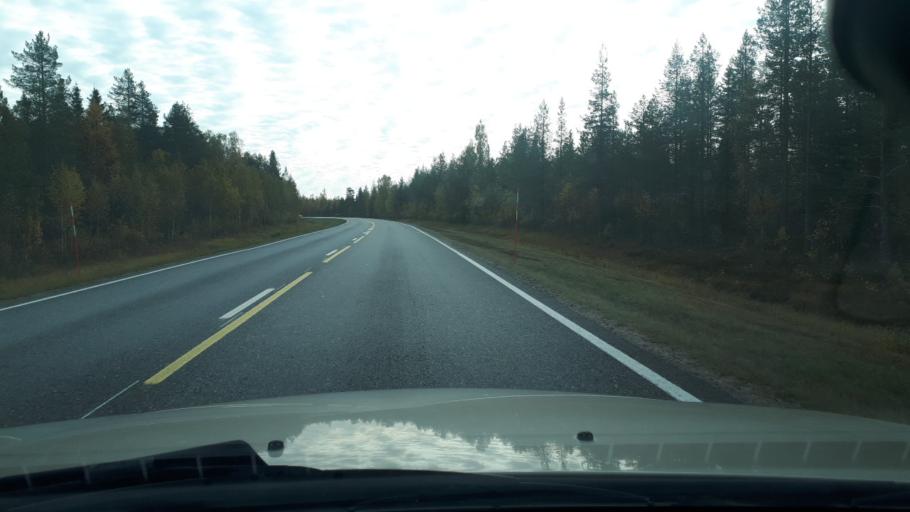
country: FI
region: Lapland
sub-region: Rovaniemi
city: Ranua
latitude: 65.9835
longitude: 26.3572
